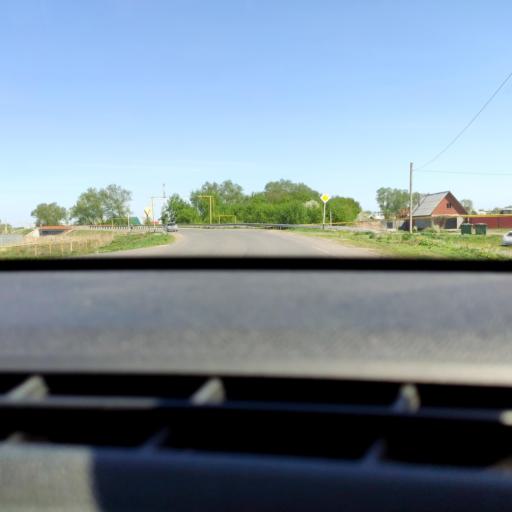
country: RU
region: Samara
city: Tol'yatti
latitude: 53.6815
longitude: 49.4278
